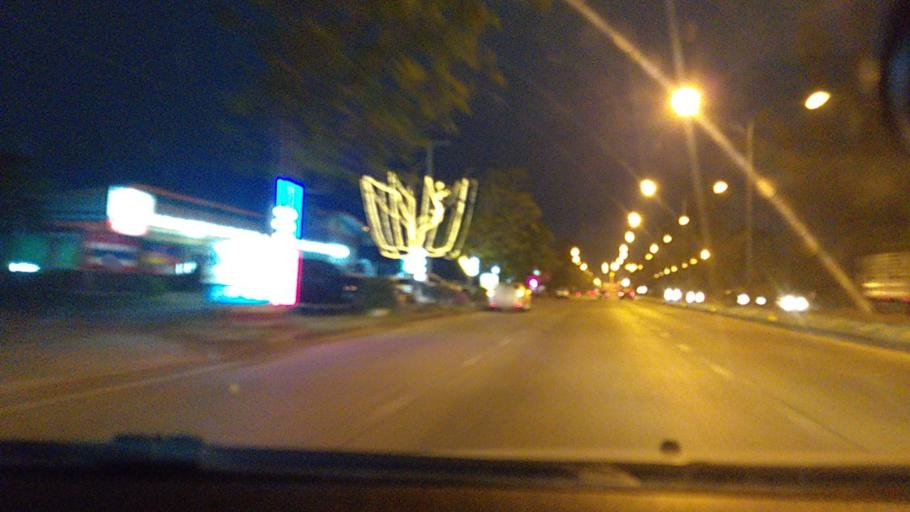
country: TH
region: Sing Buri
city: Sing Buri
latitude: 14.8708
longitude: 100.4159
